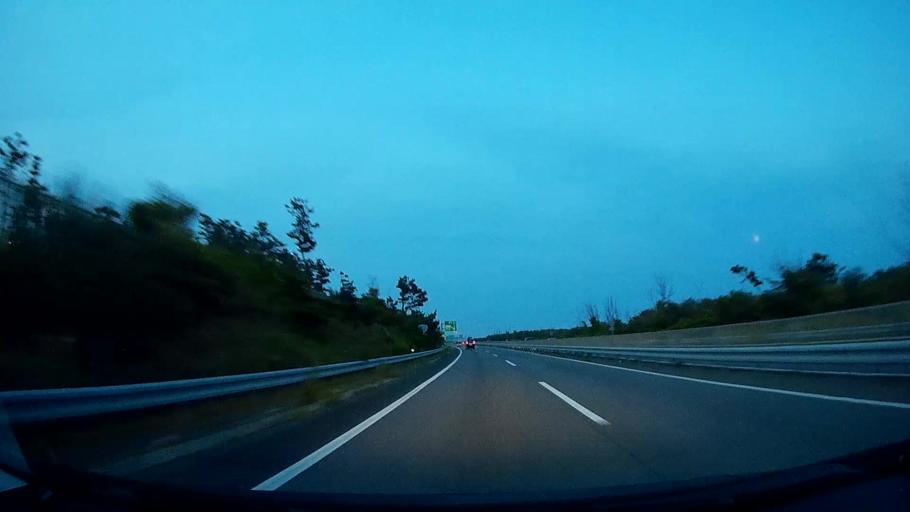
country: JP
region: Shizuoka
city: Hamamatsu
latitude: 34.6764
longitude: 137.6373
